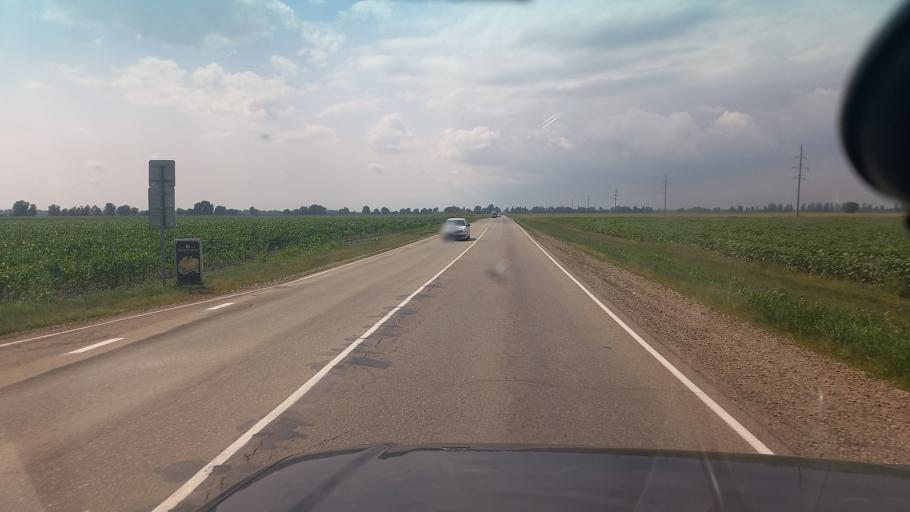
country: RU
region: Adygeya
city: Koshekhabl'
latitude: 44.9043
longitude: 40.4683
